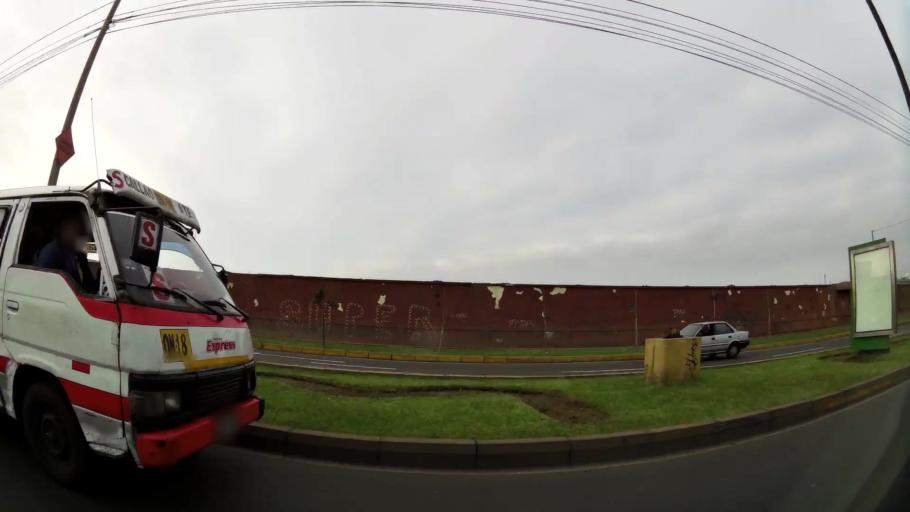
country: PE
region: Lima
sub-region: Lima
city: San Isidro
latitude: -12.1090
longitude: -77.0528
